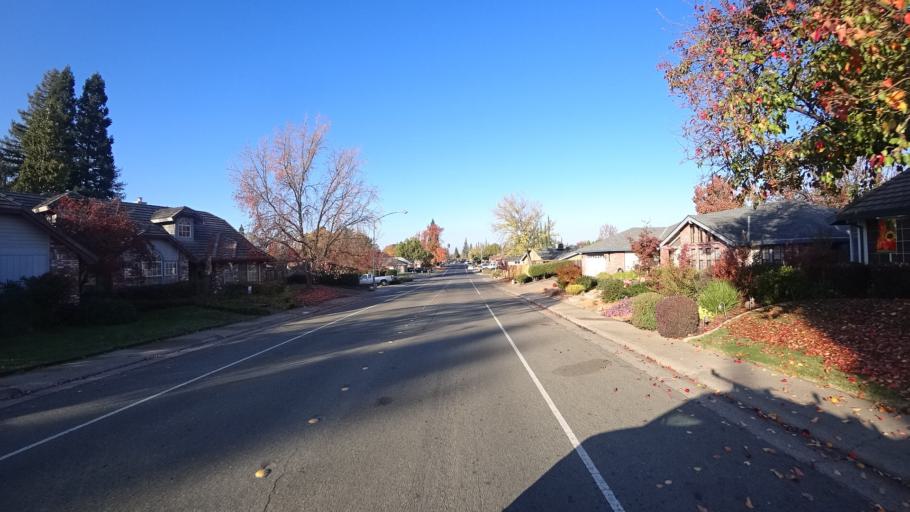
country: US
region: California
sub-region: Sacramento County
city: Citrus Heights
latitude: 38.7194
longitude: -121.2533
